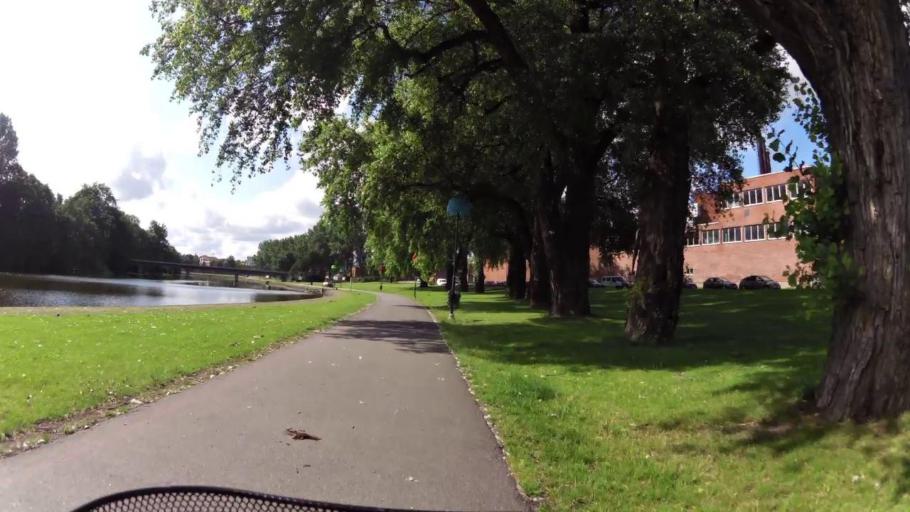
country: SE
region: OEstergoetland
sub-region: Linkopings Kommun
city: Linkoping
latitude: 58.4196
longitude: 15.6278
